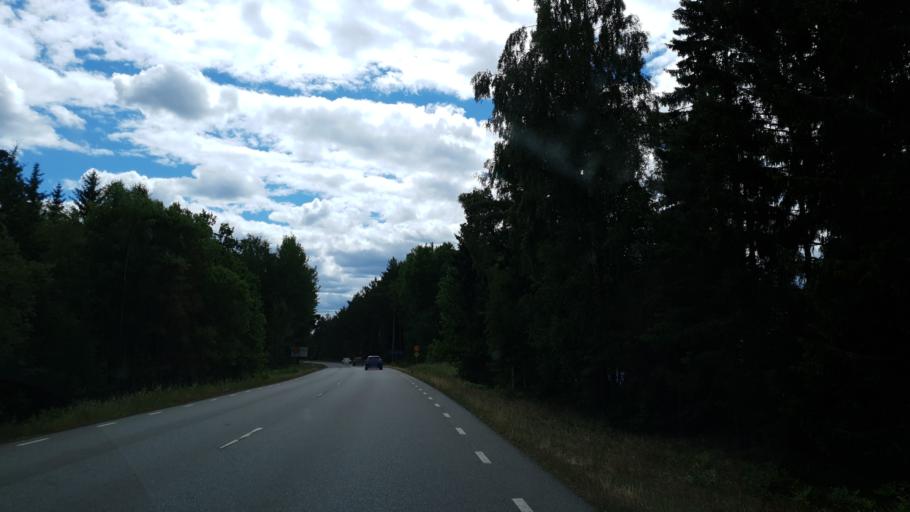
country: SE
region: Kalmar
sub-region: Emmaboda Kommun
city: Emmaboda
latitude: 56.9251
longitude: 15.5722
